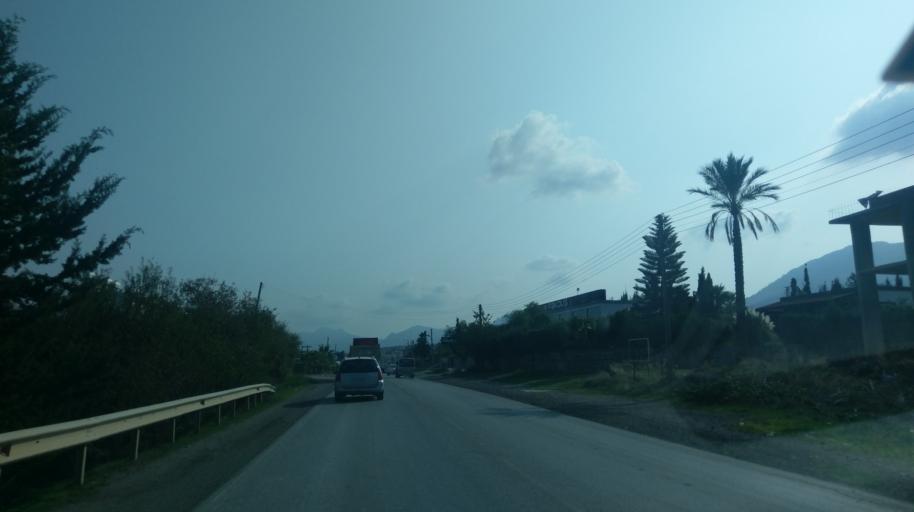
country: CY
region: Keryneia
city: Kyrenia
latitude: 35.3261
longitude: 33.3945
